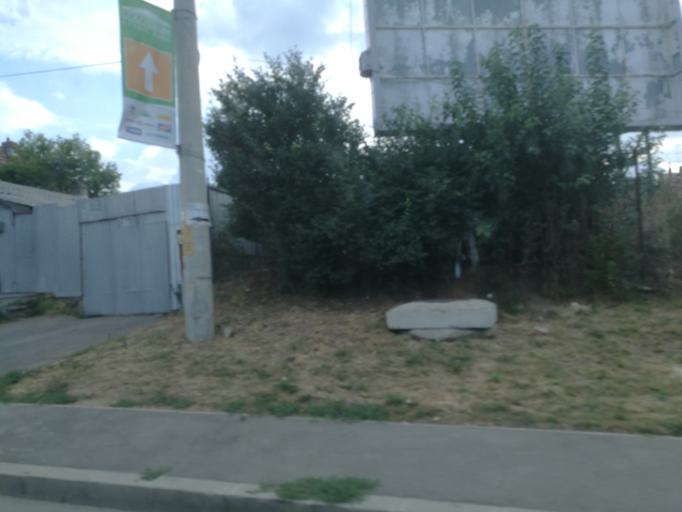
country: RO
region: Ilfov
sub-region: Comuna Mogosoaia
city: Mogosoaia
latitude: 44.5028
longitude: 26.0252
